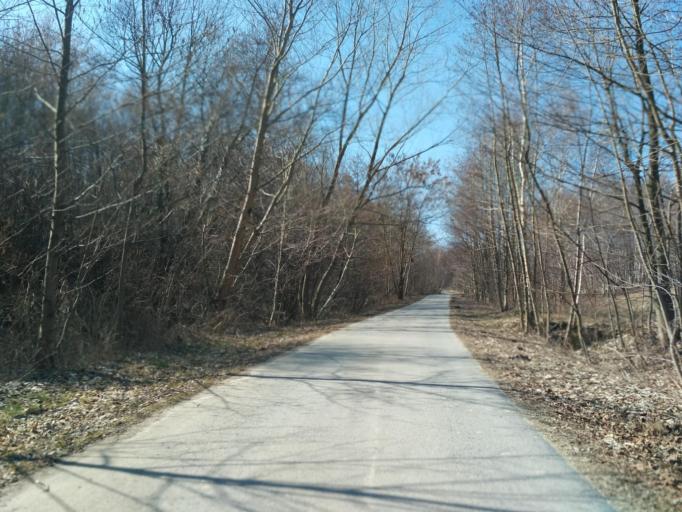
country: PL
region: Subcarpathian Voivodeship
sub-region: Powiat rzeszowski
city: Niechobrz
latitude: 49.9710
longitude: 21.8808
